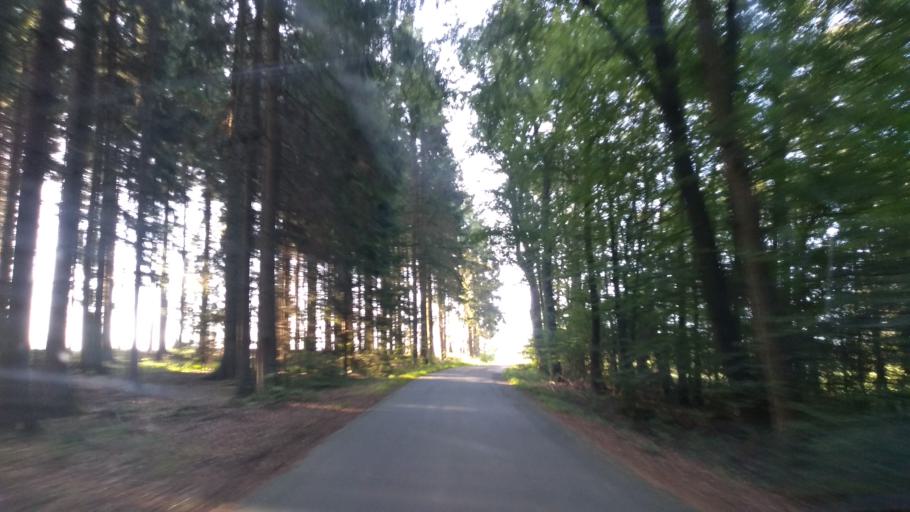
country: DE
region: North Rhine-Westphalia
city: Wiehl
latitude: 50.9527
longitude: 7.4885
